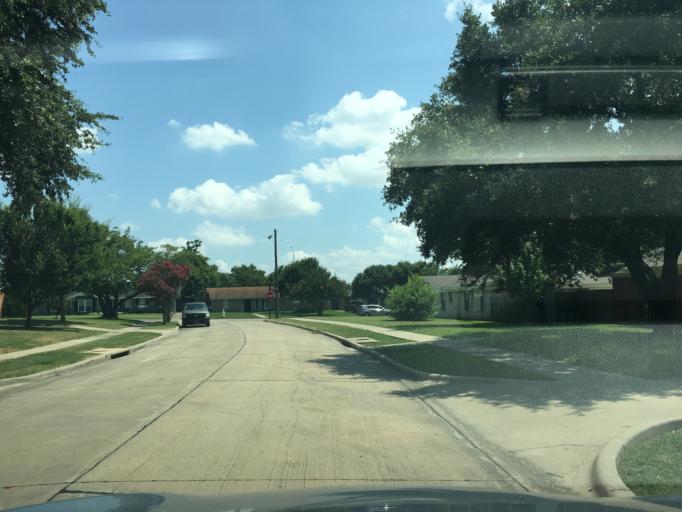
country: US
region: Texas
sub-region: Dallas County
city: Farmers Branch
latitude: 32.9191
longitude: -96.8595
